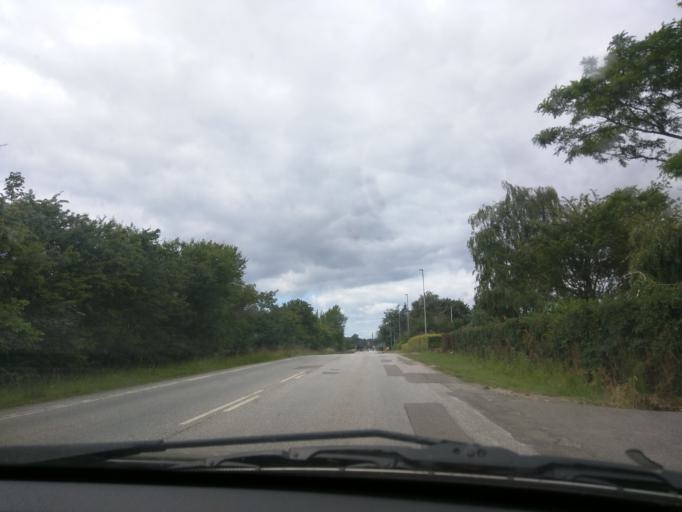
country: DK
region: Zealand
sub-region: Kalundborg Kommune
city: Kalundborg
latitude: 55.6802
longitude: 11.1272
